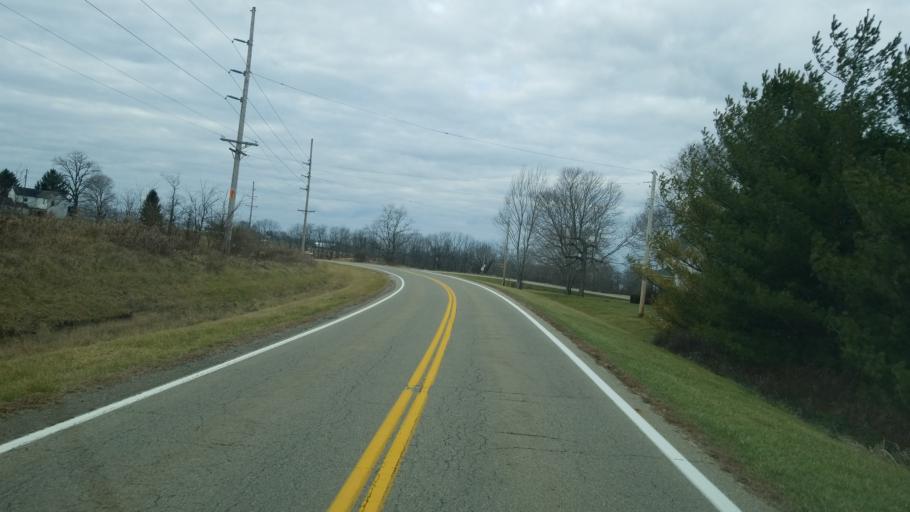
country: US
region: Ohio
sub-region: Ross County
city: Frankfort
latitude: 39.3563
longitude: -83.2741
